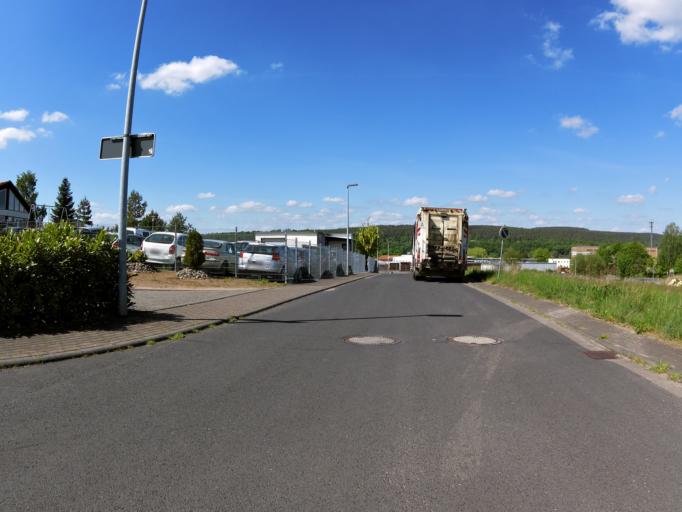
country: DE
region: Thuringia
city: Leimbach
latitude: 50.8095
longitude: 10.2125
